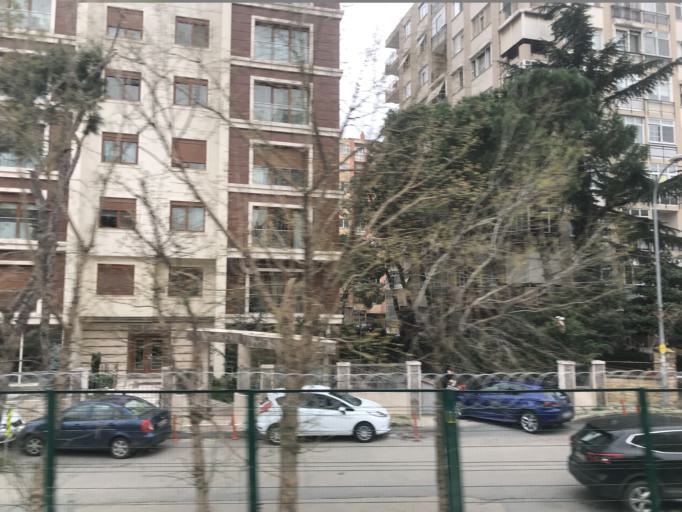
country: TR
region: Istanbul
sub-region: Atasehir
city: Atasehir
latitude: 40.9754
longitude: 29.0724
